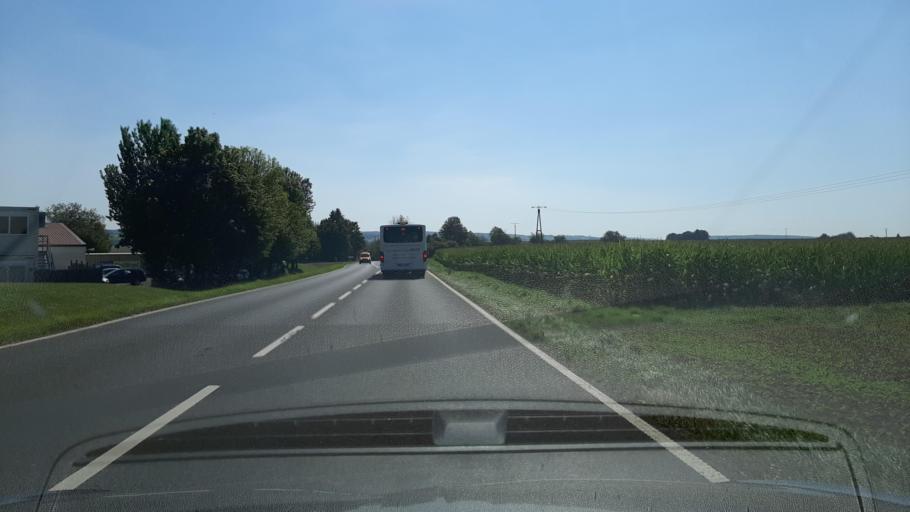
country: DE
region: Rheinland-Pfalz
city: Dudeldorf
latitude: 49.9752
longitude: 6.6271
